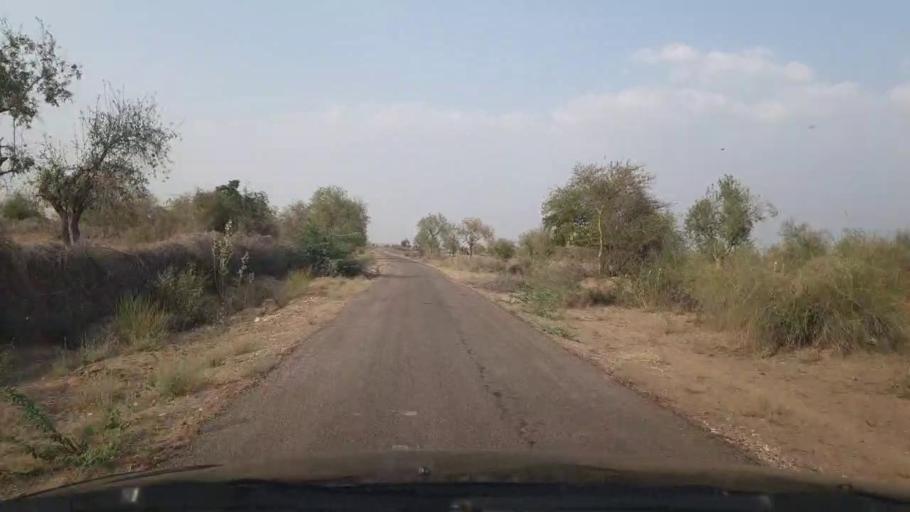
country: PK
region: Sindh
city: Islamkot
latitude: 25.0439
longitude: 70.5568
